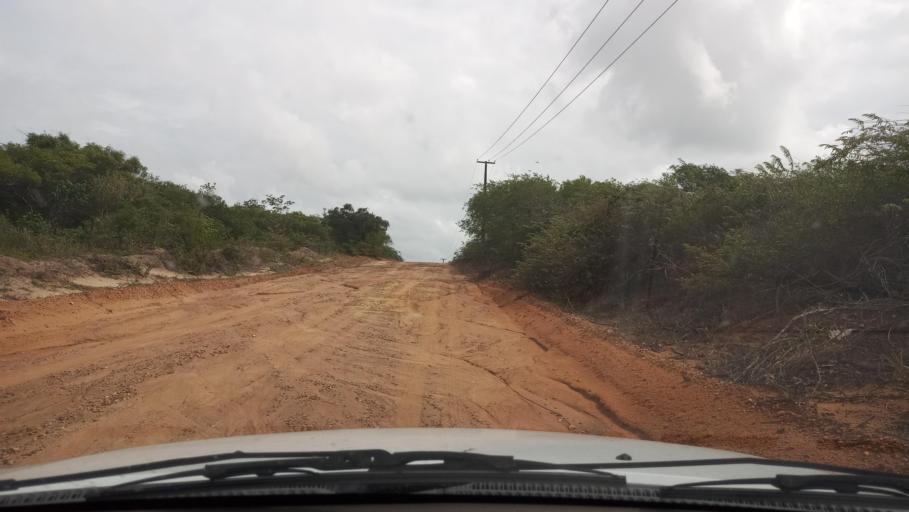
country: BR
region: Rio Grande do Norte
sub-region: Maxaranguape
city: Sao Miguel
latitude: -5.4810
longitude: -35.3032
